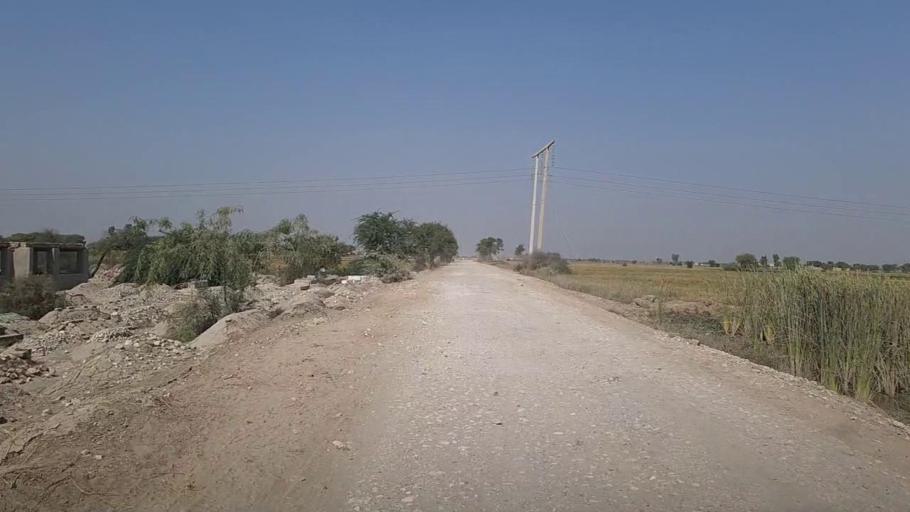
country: PK
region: Sindh
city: Kandhkot
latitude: 28.3914
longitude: 69.3266
